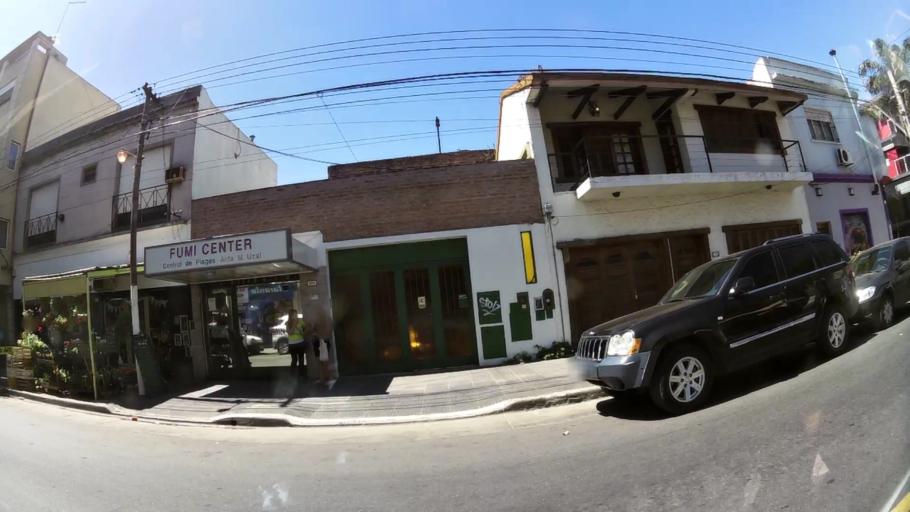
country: AR
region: Buenos Aires
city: Caseros
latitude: -34.5983
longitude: -58.5434
